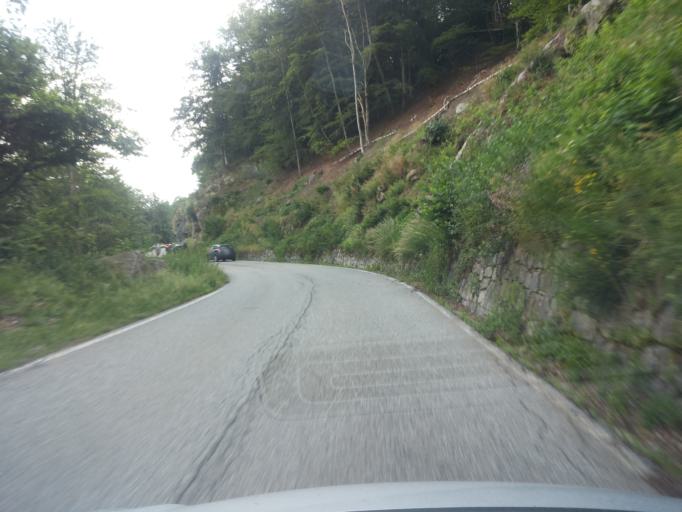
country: IT
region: Piedmont
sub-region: Provincia di Biella
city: Quittengo
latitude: 45.6589
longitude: 8.0213
